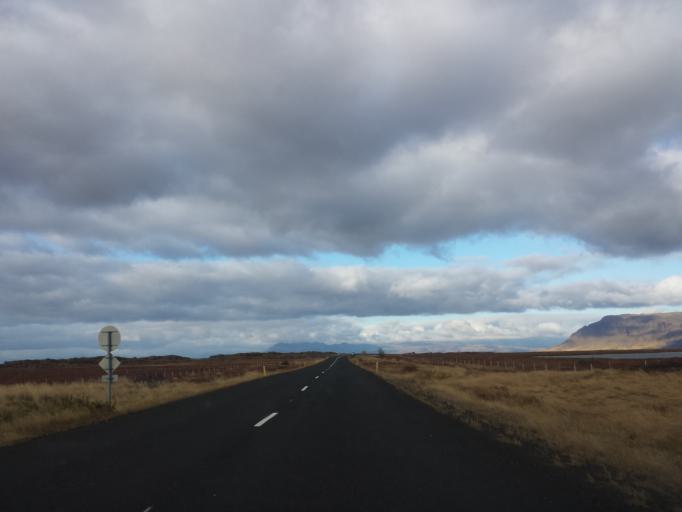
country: IS
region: West
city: Borgarnes
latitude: 64.6851
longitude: -22.0893
